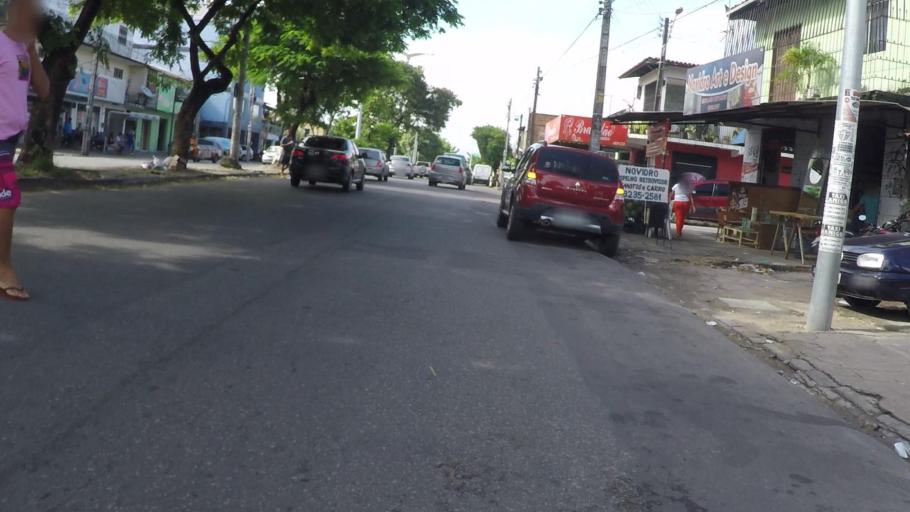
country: BR
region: Ceara
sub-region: Fortaleza
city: Fortaleza
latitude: -3.7343
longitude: -38.5844
